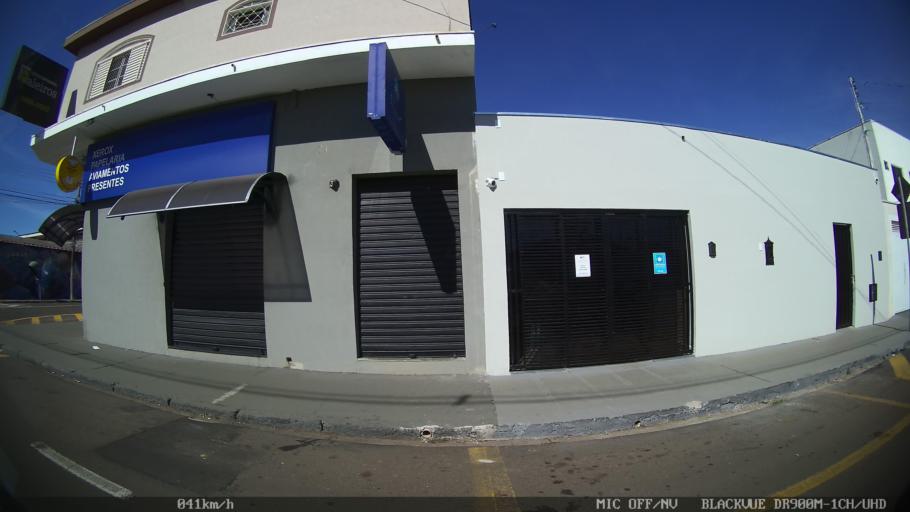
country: BR
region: Sao Paulo
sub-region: Franca
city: Franca
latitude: -20.5440
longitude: -47.3856
